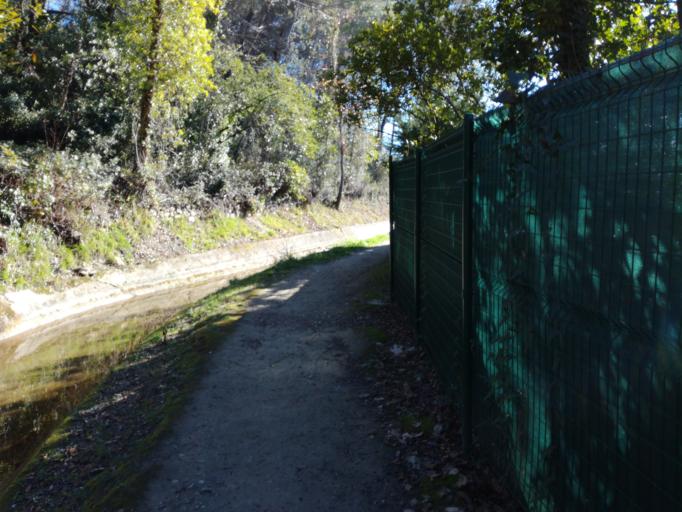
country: FR
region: Provence-Alpes-Cote d'Azur
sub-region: Departement des Alpes-Maritimes
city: Mouans-Sartoux
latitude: 43.6277
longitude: 6.9796
